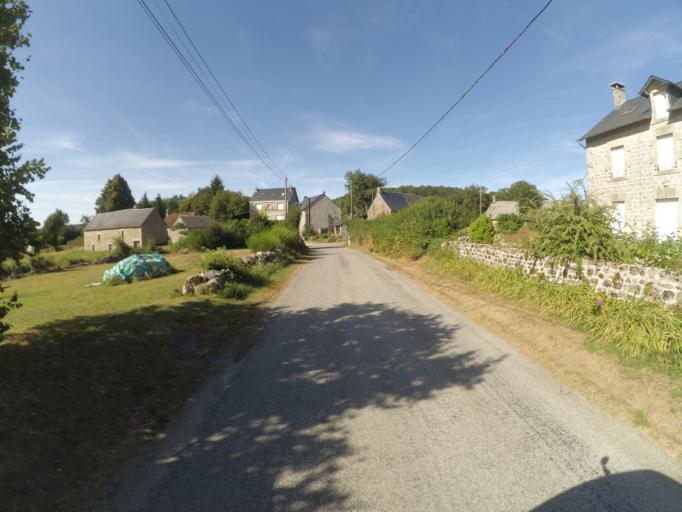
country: FR
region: Limousin
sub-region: Departement de la Correze
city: Bugeat
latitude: 45.7005
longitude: 1.8784
